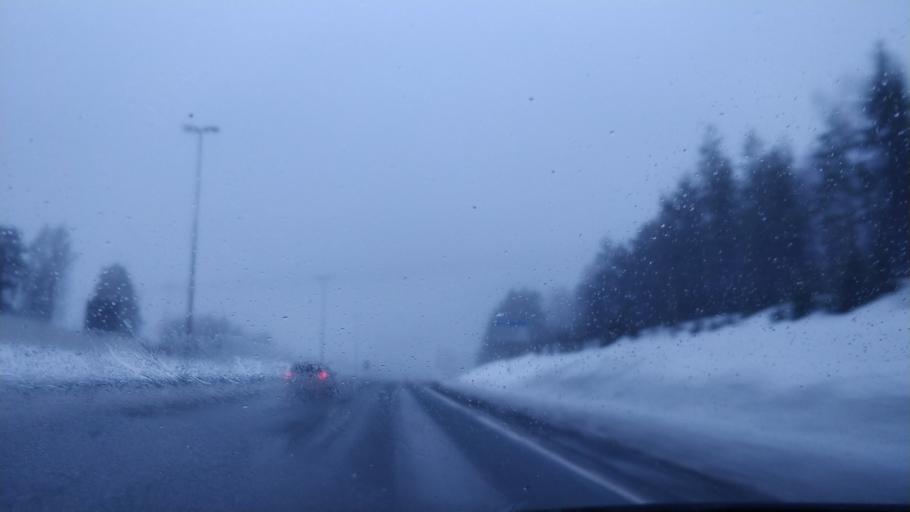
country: FI
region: Lapland
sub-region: Kemi-Tornio
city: Kemi
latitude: 65.7523
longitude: 24.5744
